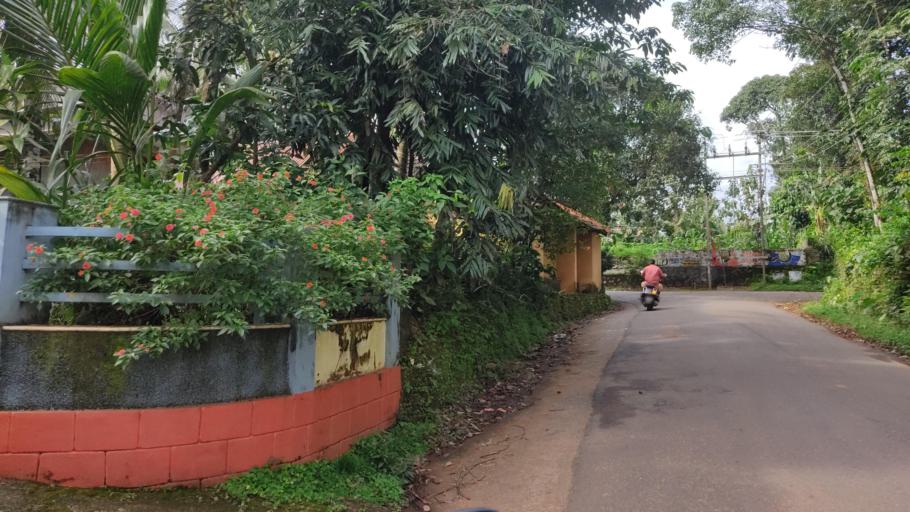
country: IN
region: Kerala
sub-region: Pattanamtitta
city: Adur
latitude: 9.1989
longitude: 76.7789
